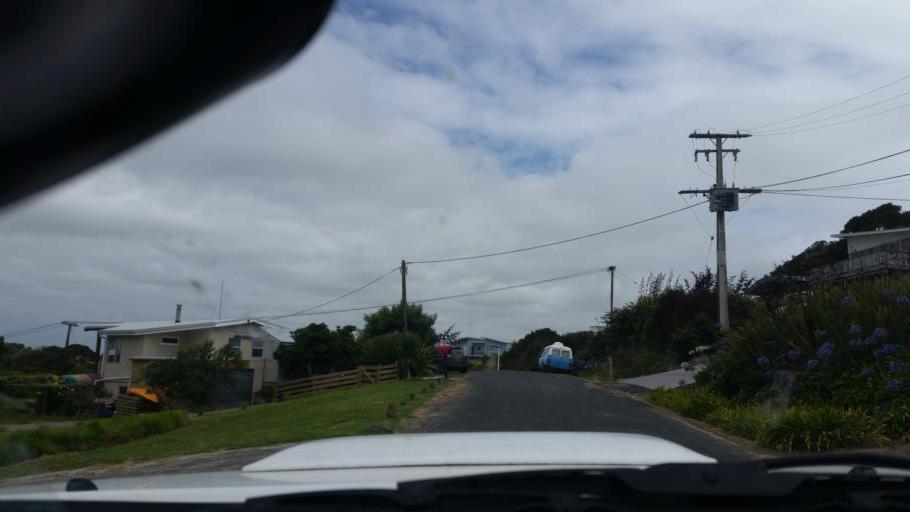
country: NZ
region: Auckland
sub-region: Auckland
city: Wellsford
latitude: -36.1566
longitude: 174.2374
